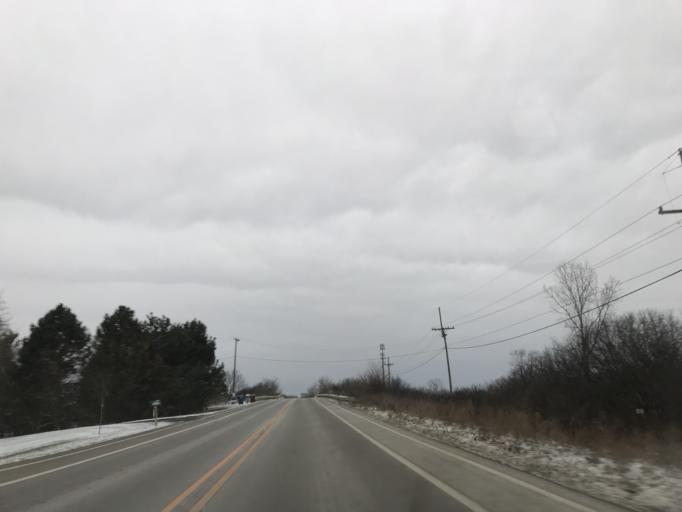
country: US
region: Michigan
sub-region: Washtenaw County
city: Ann Arbor
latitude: 42.3181
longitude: -83.7347
